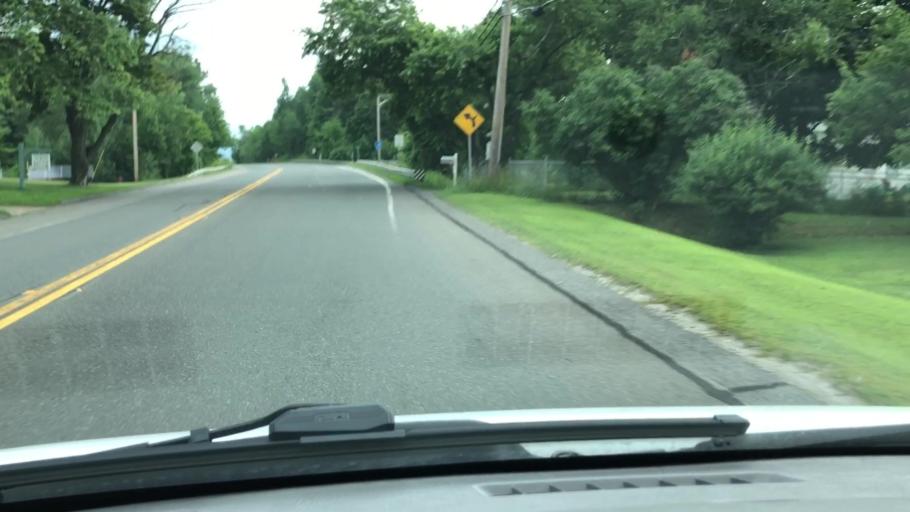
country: US
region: Massachusetts
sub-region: Berkshire County
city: Adams
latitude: 42.5841
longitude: -73.1470
